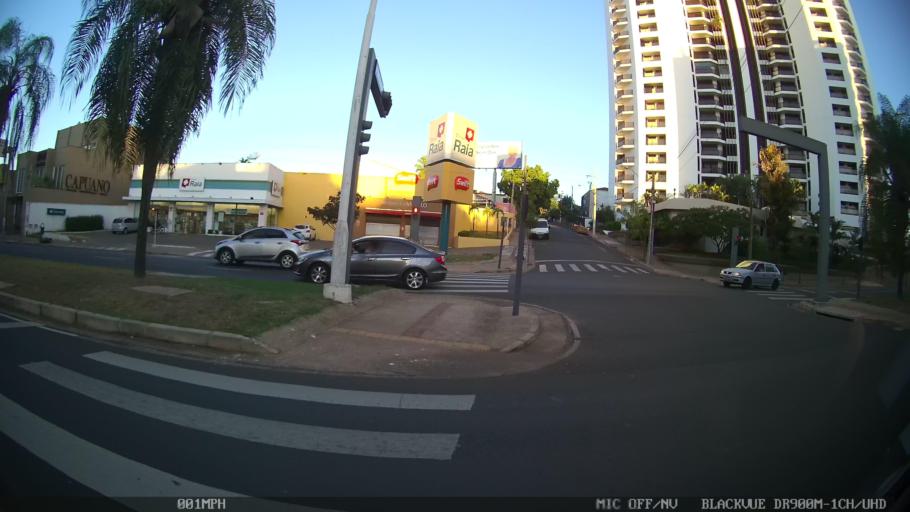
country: BR
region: Sao Paulo
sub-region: Sao Jose Do Rio Preto
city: Sao Jose do Rio Preto
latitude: -20.8207
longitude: -49.3835
